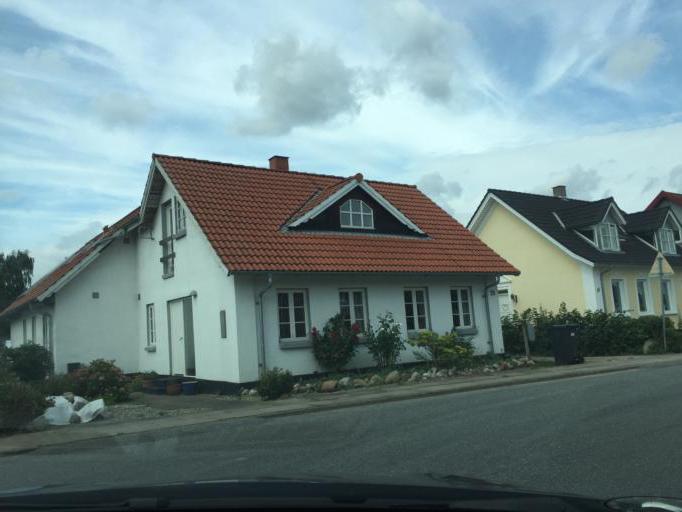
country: DK
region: South Denmark
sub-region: Assens Kommune
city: Vissenbjerg
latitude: 55.3651
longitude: 10.1450
